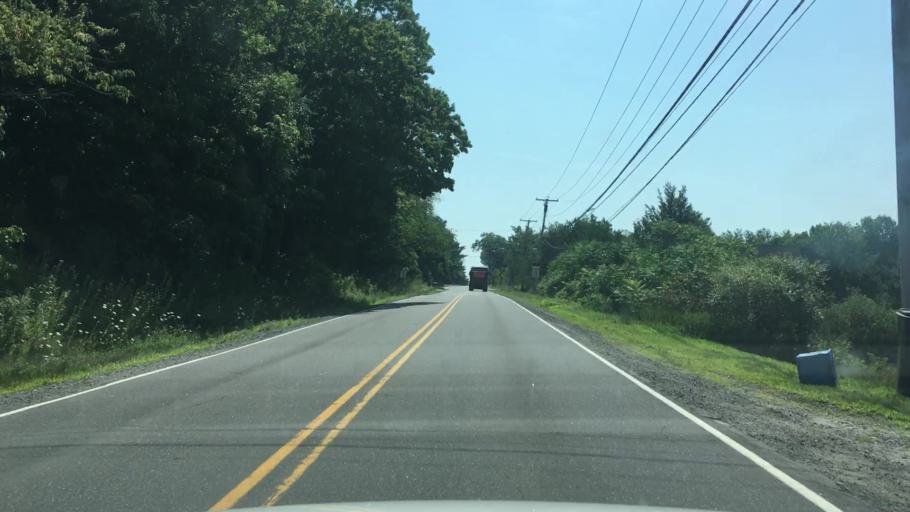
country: US
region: Maine
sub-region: Kennebec County
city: Hallowell
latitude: 44.2947
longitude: -69.8025
